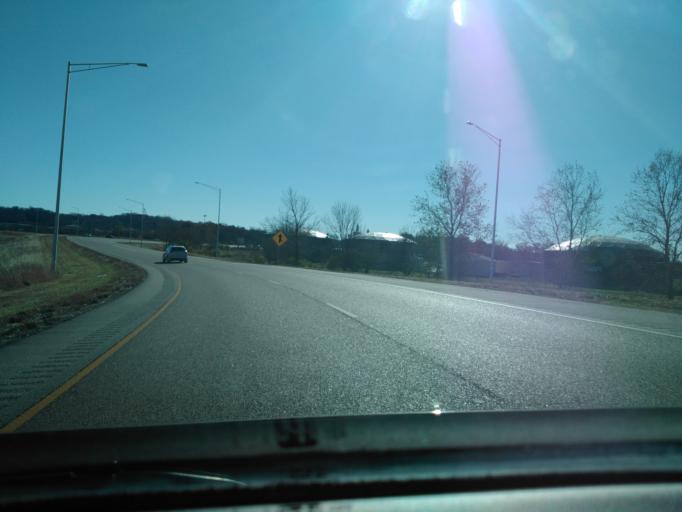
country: US
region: Illinois
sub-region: Saint Clair County
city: Caseyville
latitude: 38.6703
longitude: -90.0327
